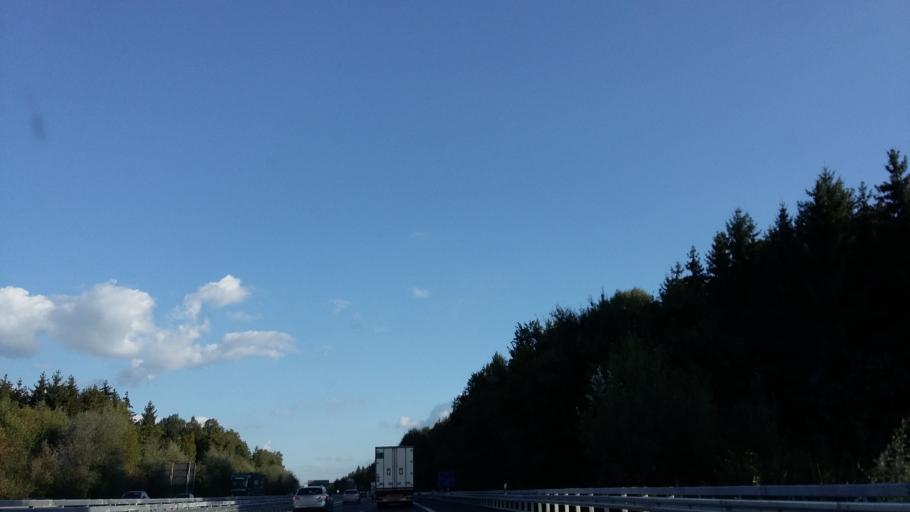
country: DE
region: Bavaria
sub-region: Swabia
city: Vohringen
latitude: 48.3136
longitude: 10.0935
